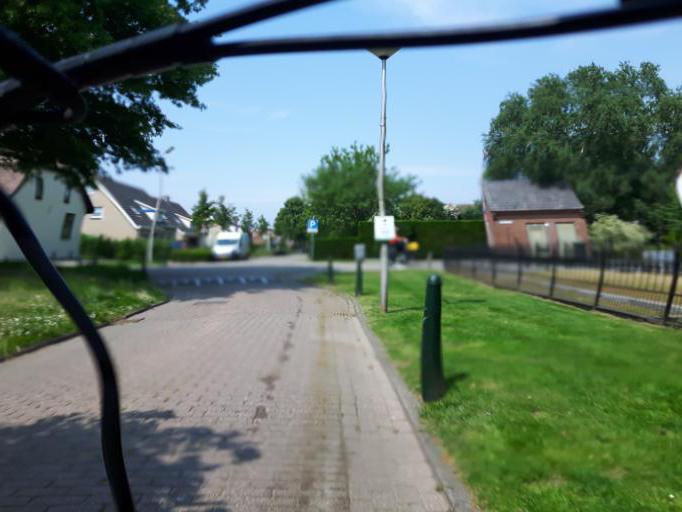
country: NL
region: North Brabant
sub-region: Gemeente Steenbergen
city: Welberg
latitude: 51.5774
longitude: 4.3334
